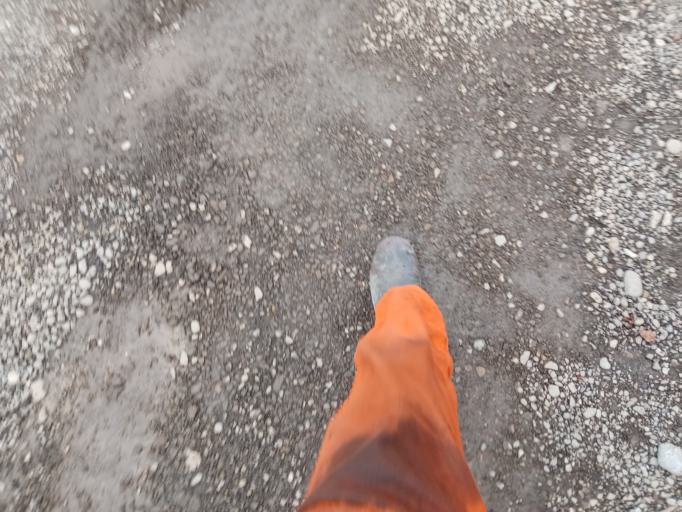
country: GE
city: Zahesi
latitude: 41.7953
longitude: 44.7729
